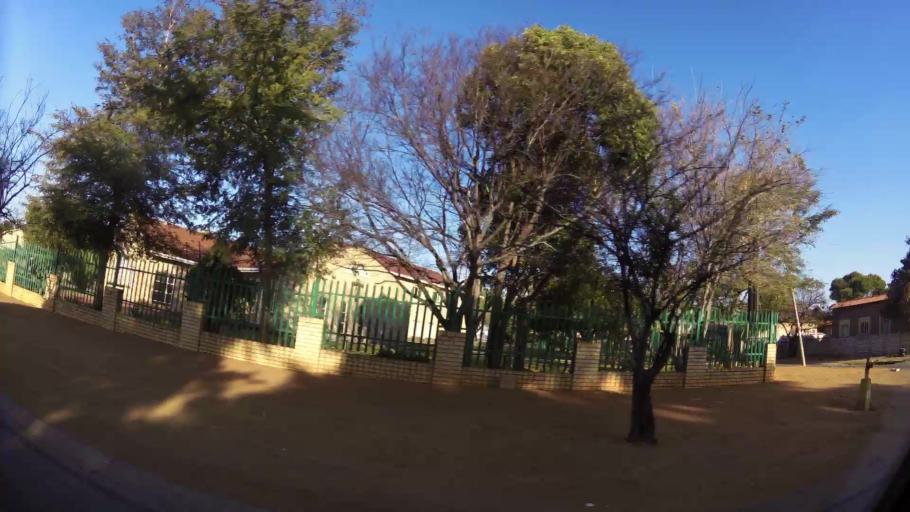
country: ZA
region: North-West
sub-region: Bojanala Platinum District Municipality
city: Rustenburg
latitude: -25.6798
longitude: 27.2170
